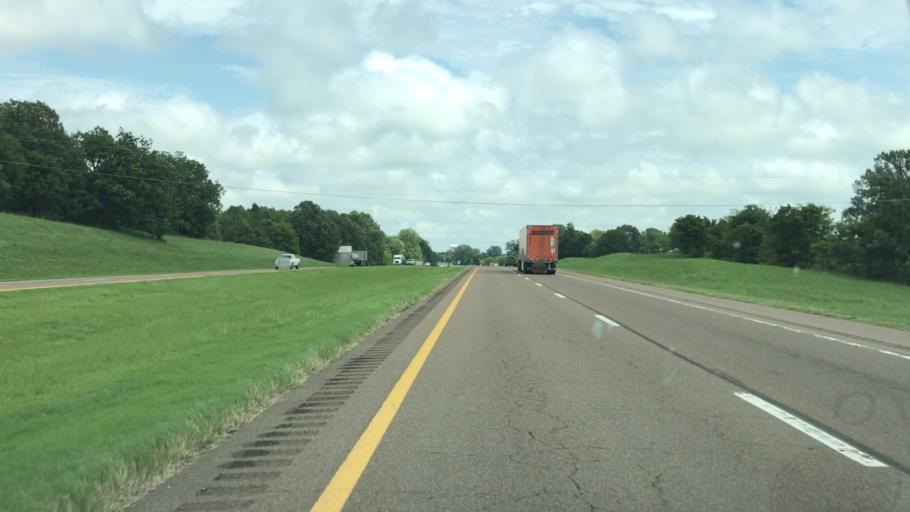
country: US
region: Tennessee
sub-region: Dyer County
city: Dyersburg
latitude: 36.0680
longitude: -89.3694
